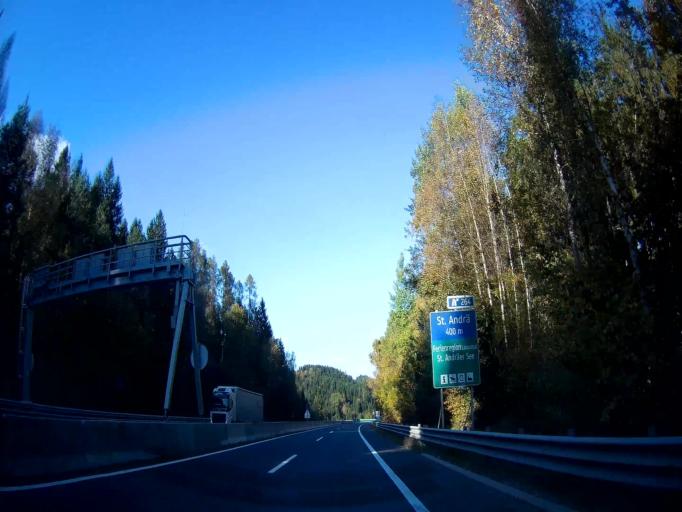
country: AT
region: Carinthia
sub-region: Politischer Bezirk Wolfsberg
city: Sankt Andrae
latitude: 46.7379
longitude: 14.8041
